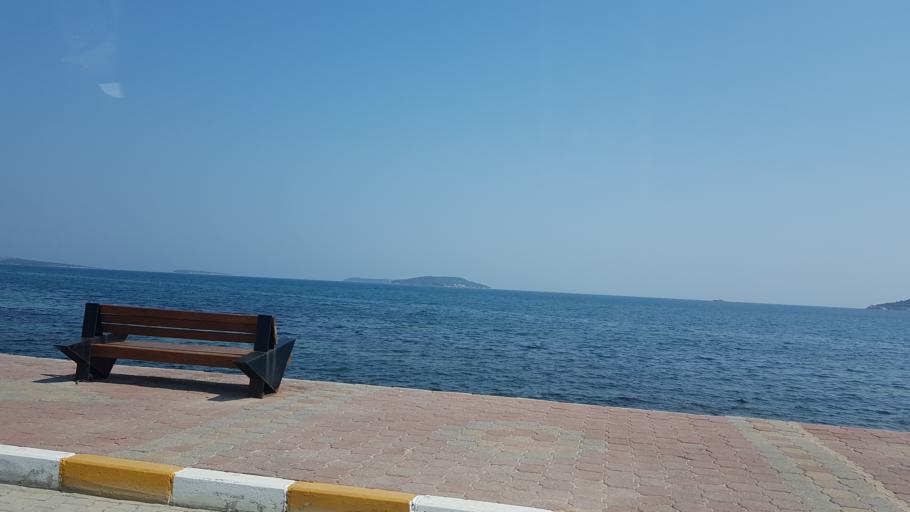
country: TR
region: Izmir
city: Urla
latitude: 38.3699
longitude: 26.7639
